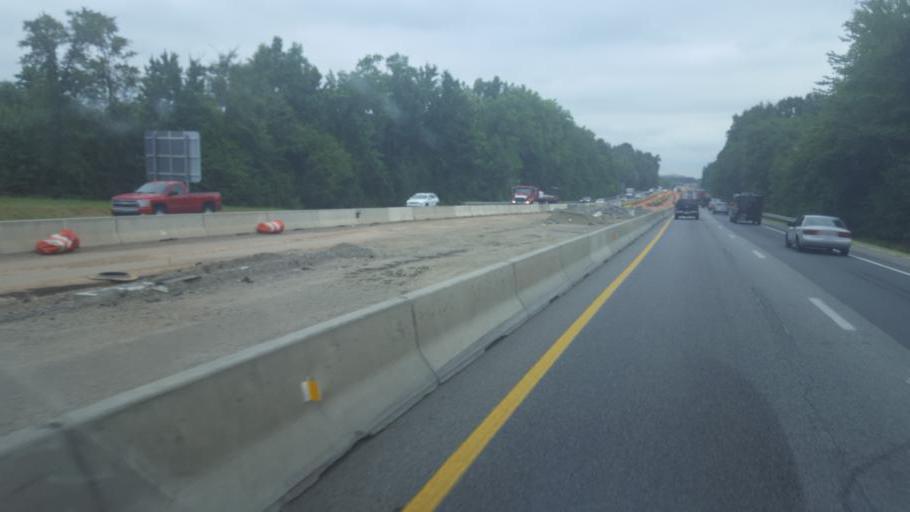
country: US
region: North Carolina
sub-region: Mecklenburg County
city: Cornelius
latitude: 35.4900
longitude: -80.8727
